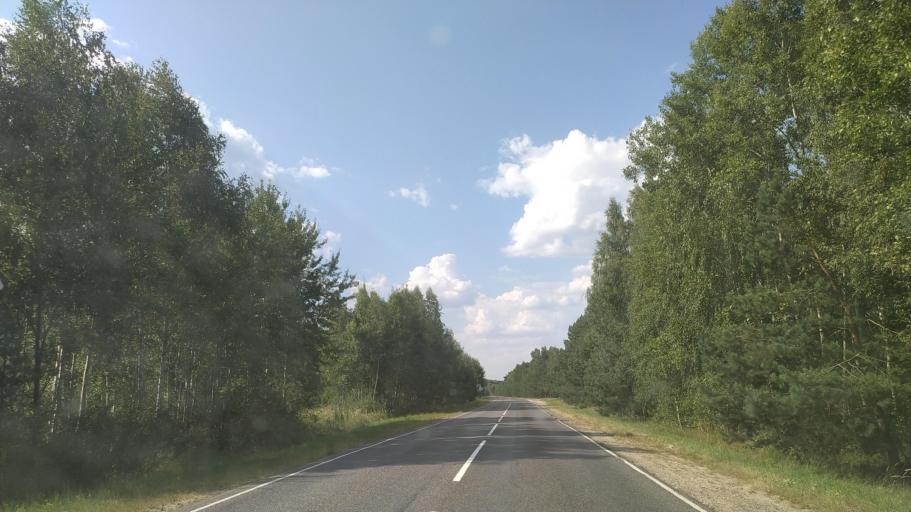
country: BY
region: Brest
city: Drahichyn
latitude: 52.2227
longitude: 25.1230
